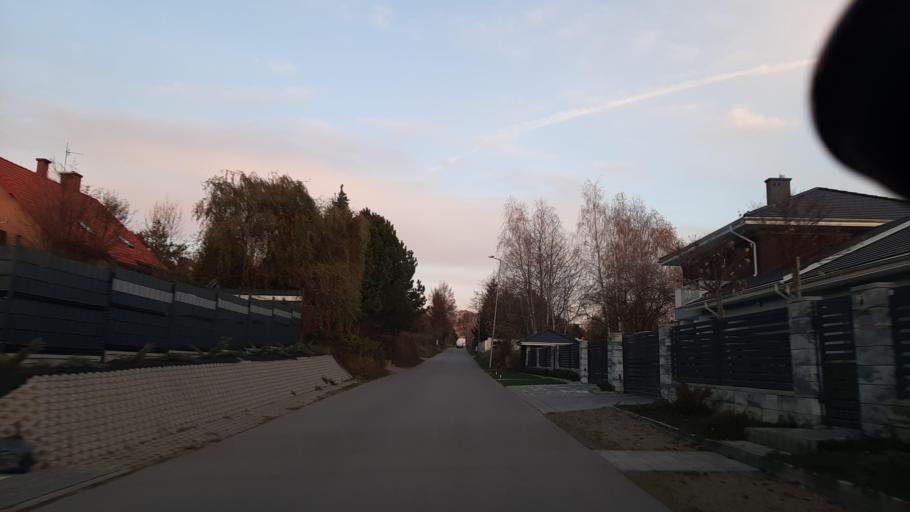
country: PL
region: Lublin Voivodeship
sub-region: Powiat lubelski
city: Jastkow
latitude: 51.2919
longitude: 22.5000
